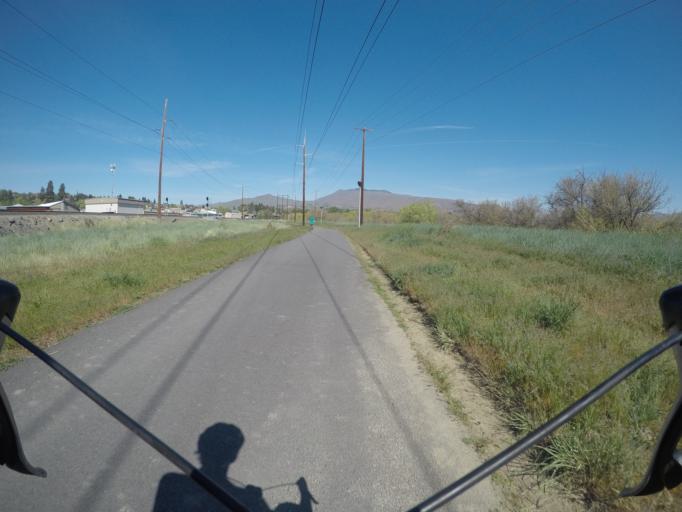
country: US
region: Washington
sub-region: Chelan County
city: Sunnyslope
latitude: 47.4533
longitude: -120.3316
